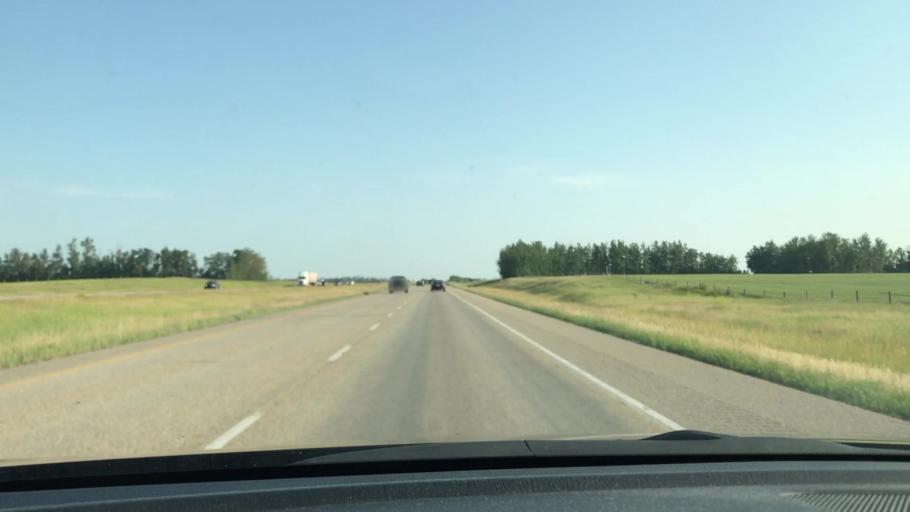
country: CA
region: Alberta
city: Millet
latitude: 53.1152
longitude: -113.5984
